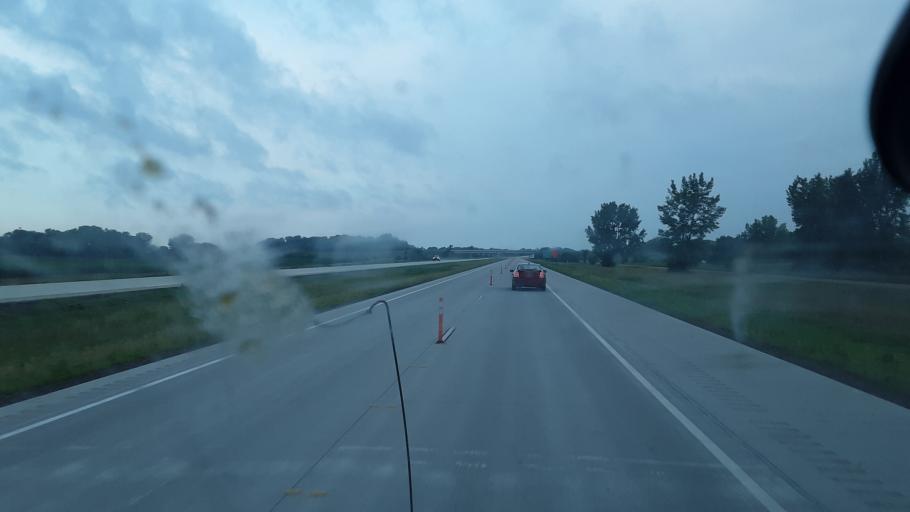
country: US
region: Minnesota
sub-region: Martin County
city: Fairmont
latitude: 43.6707
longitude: -94.3993
